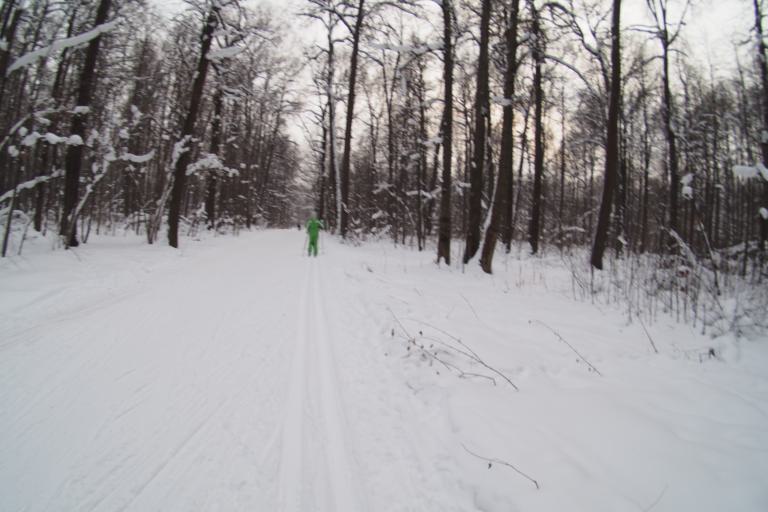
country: RU
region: Moskovskaya
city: Izmaylovo
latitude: 55.7683
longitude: 37.7774
